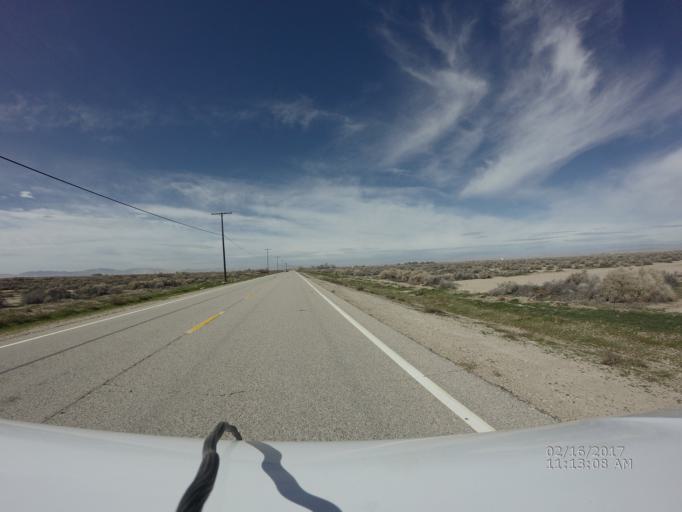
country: US
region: California
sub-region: Los Angeles County
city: Lake Los Angeles
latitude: 34.7194
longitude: -117.9371
